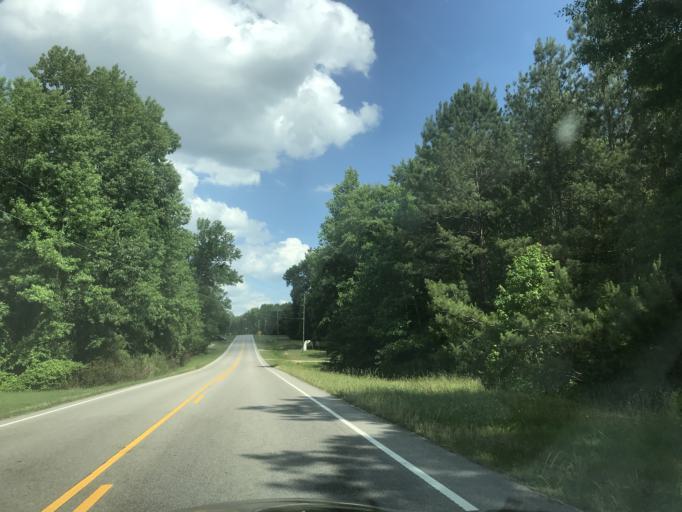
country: US
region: North Carolina
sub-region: Franklin County
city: Louisburg
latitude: 35.9603
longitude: -78.2802
